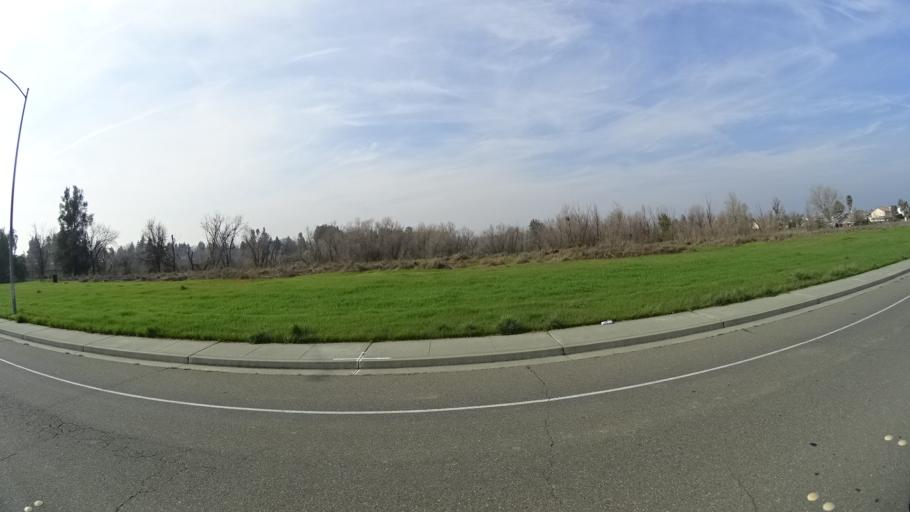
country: US
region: California
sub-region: Yolo County
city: Davis
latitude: 38.5720
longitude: -121.7468
